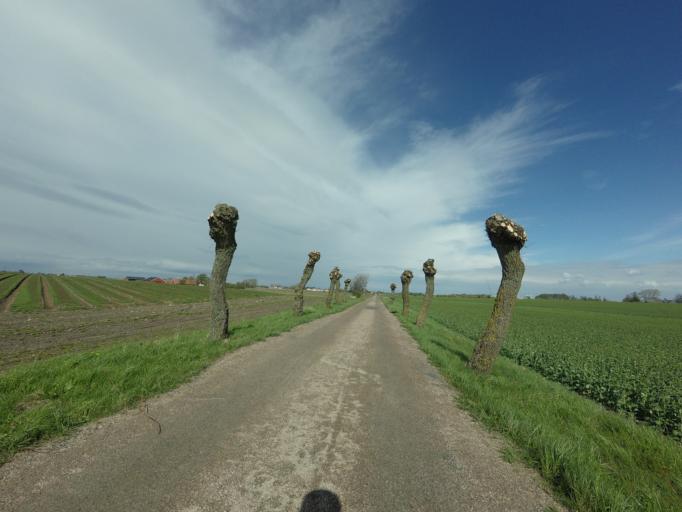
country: SE
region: Skane
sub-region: Malmo
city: Tygelsjo
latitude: 55.5303
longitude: 12.9818
